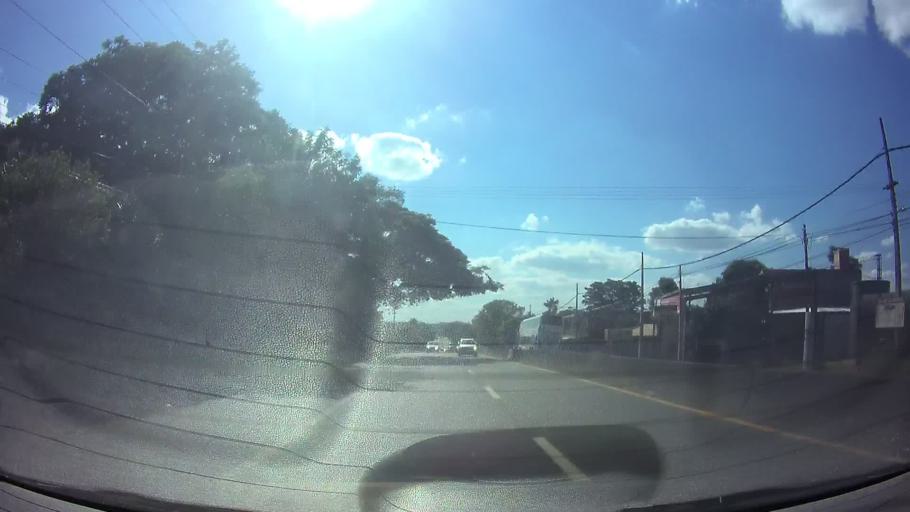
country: PY
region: Central
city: Itaugua
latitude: -25.3981
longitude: -57.3346
